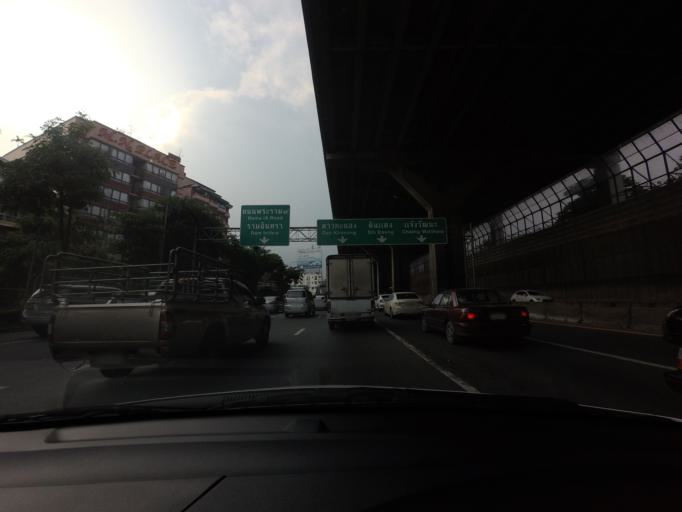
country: TH
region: Bangkok
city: Phra Khanong
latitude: 13.6952
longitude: 100.5956
